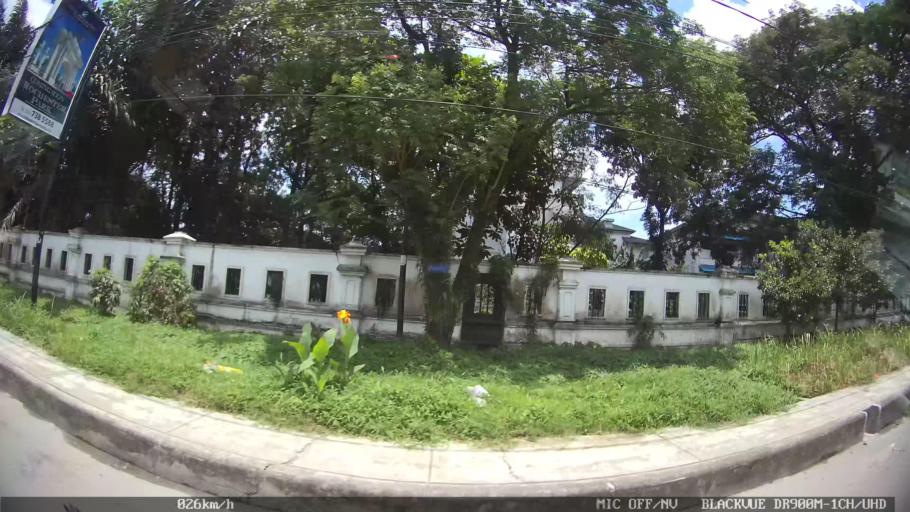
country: ID
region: North Sumatra
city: Medan
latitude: 3.6063
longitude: 98.7132
